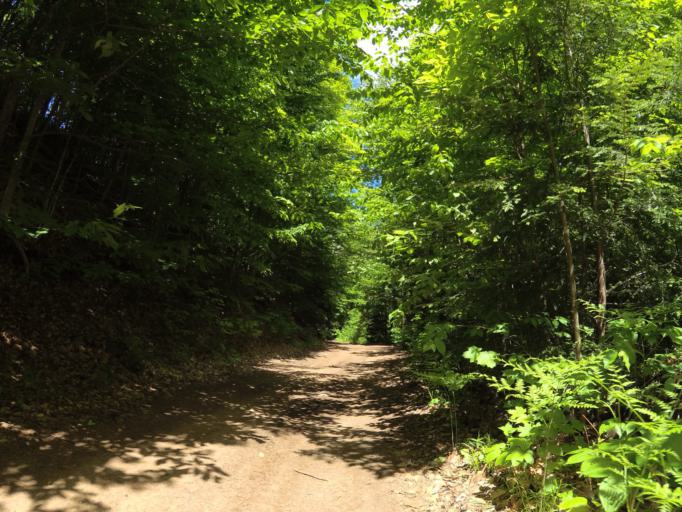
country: CA
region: Ontario
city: Renfrew
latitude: 45.0383
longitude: -76.8716
